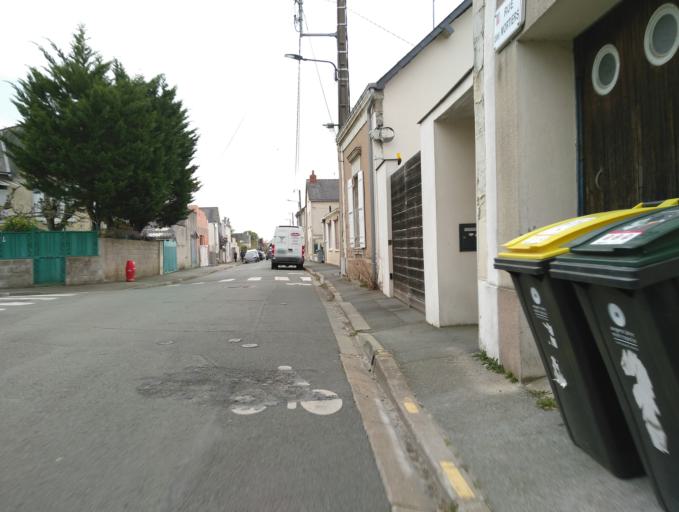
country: FR
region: Pays de la Loire
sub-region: Departement de Maine-et-Loire
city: Angers
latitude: 47.4542
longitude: -0.5285
